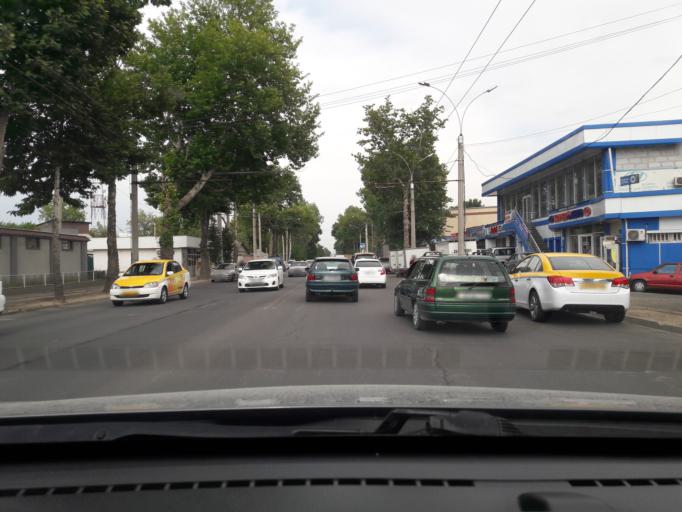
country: TJ
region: Dushanbe
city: Dushanbe
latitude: 38.5461
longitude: 68.7503
